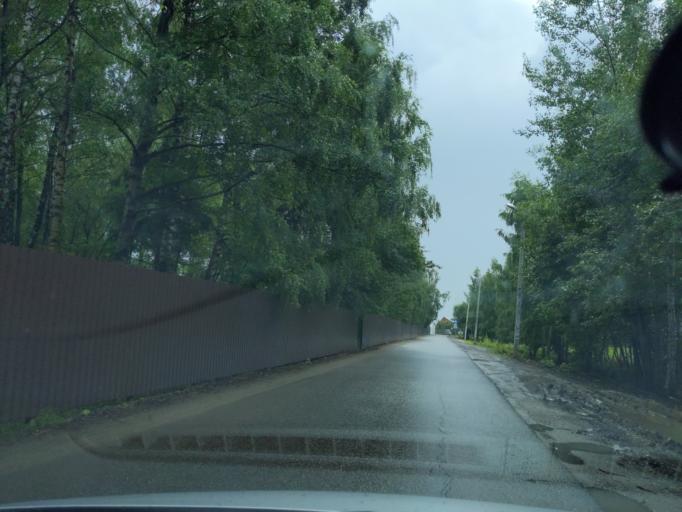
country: RU
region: Moskovskaya
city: Lugovaya
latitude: 56.0679
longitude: 37.5143
